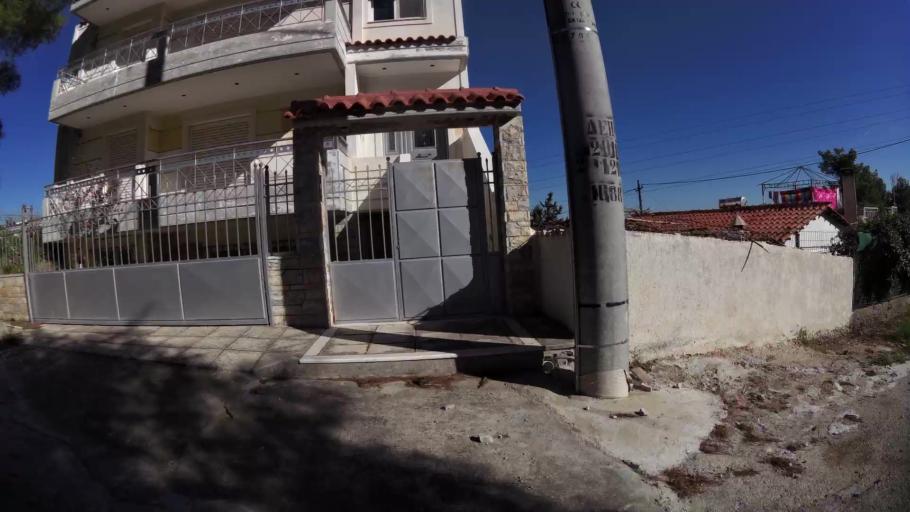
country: GR
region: Attica
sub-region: Nomarchia Anatolikis Attikis
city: Leondarion
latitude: 37.9892
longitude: 23.8422
